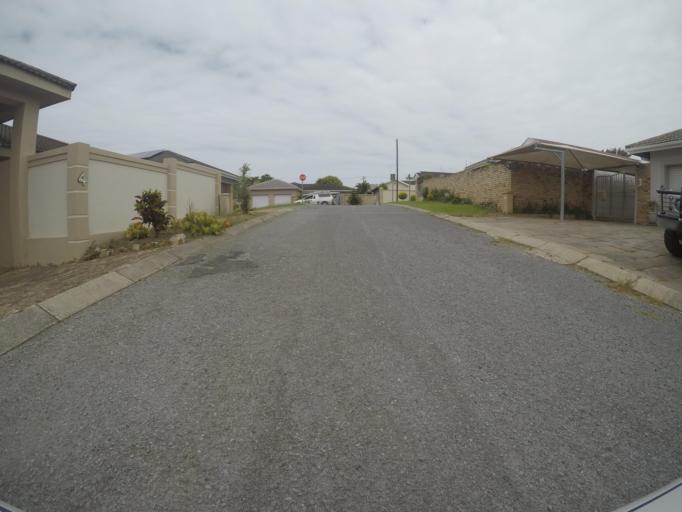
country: ZA
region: Eastern Cape
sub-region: Buffalo City Metropolitan Municipality
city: East London
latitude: -32.9767
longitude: 27.9534
